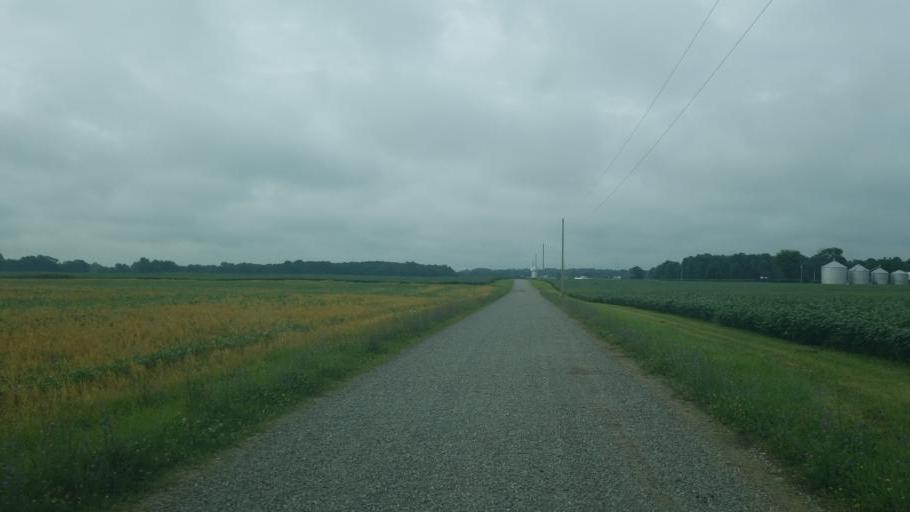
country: US
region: Ohio
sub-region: Knox County
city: Centerburg
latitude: 40.4254
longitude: -82.6795
